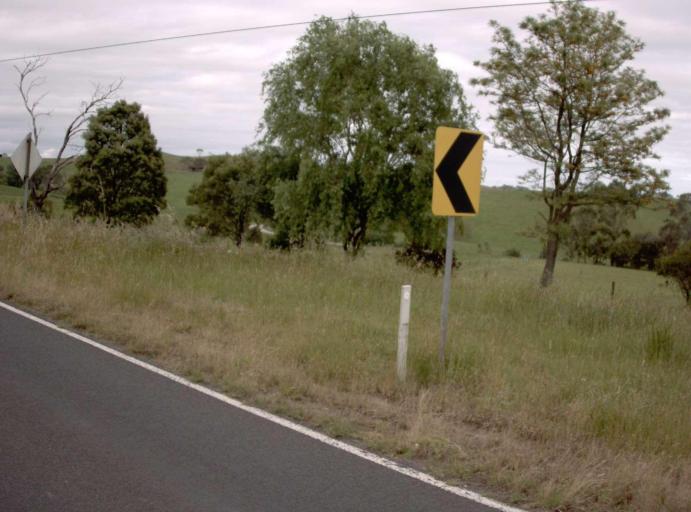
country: AU
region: Victoria
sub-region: Bass Coast
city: North Wonthaggi
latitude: -38.4445
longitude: 145.8026
